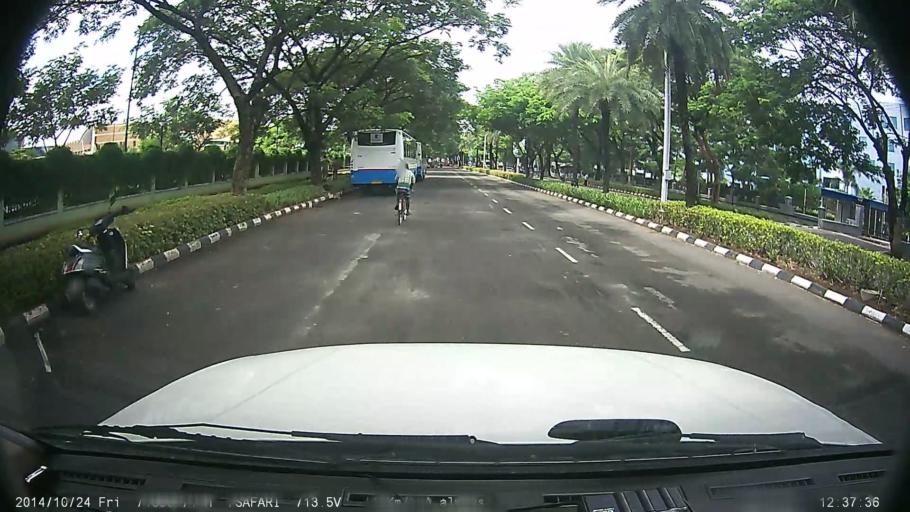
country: IN
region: Tamil Nadu
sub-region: Kancheepuram
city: Singapperumalkovil
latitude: 12.7364
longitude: 80.0066
